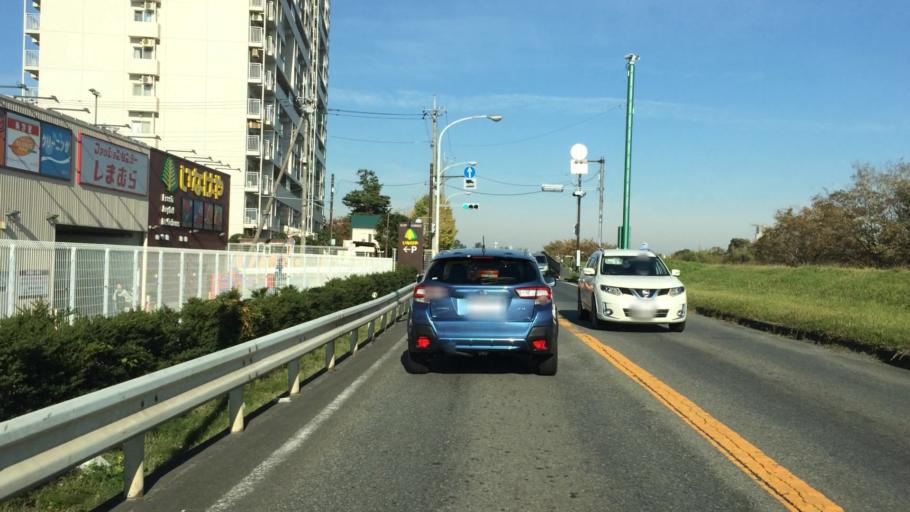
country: JP
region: Tokyo
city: Chofugaoka
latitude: 35.6292
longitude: 139.5639
